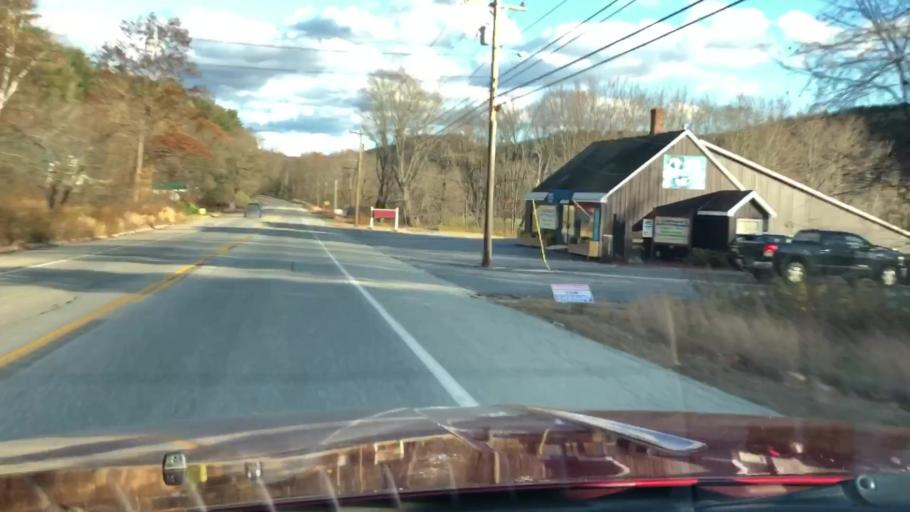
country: US
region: Maine
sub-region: Oxford County
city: Dixfield
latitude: 44.5327
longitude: -70.5012
